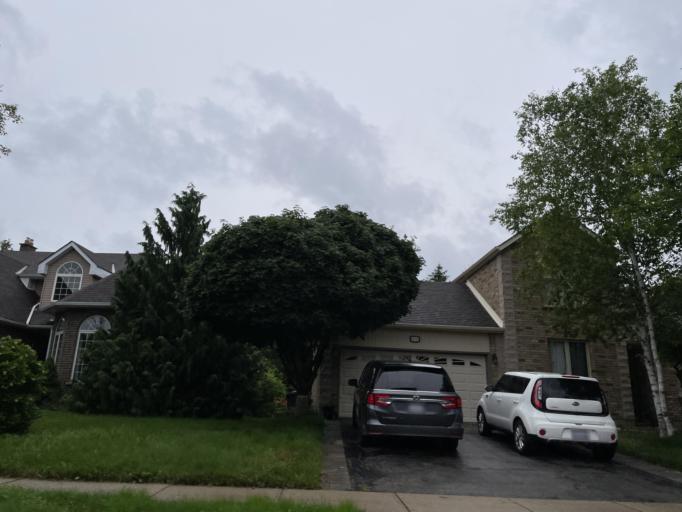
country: CA
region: Ontario
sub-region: Wellington County
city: Guelph
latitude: 43.5007
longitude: -80.2383
